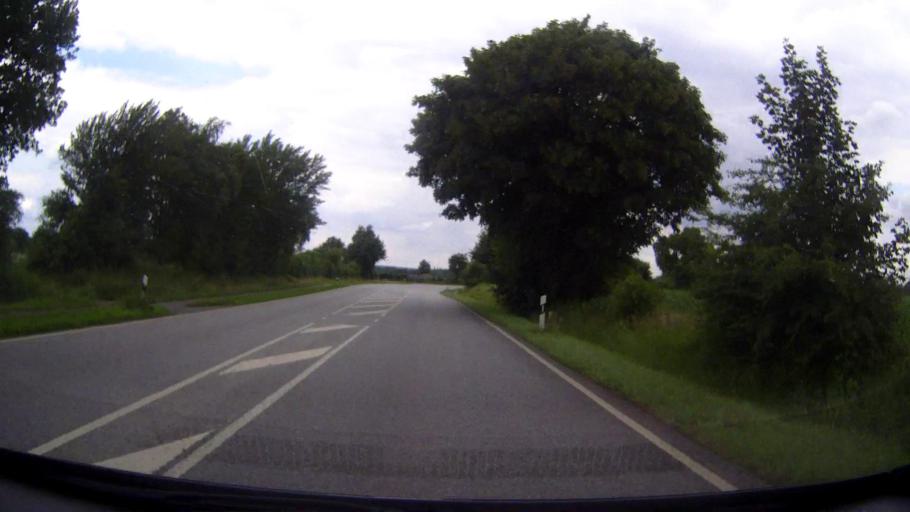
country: DE
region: Schleswig-Holstein
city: Reher
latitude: 54.0745
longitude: 9.5792
